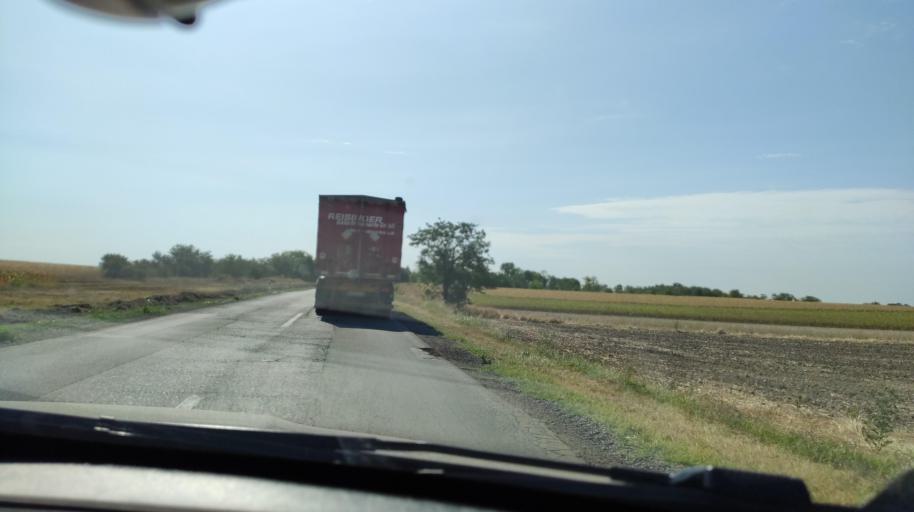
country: RS
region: Autonomna Pokrajina Vojvodina
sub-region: Severnobacki Okrug
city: Backa Topola
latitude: 45.8294
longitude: 19.5951
